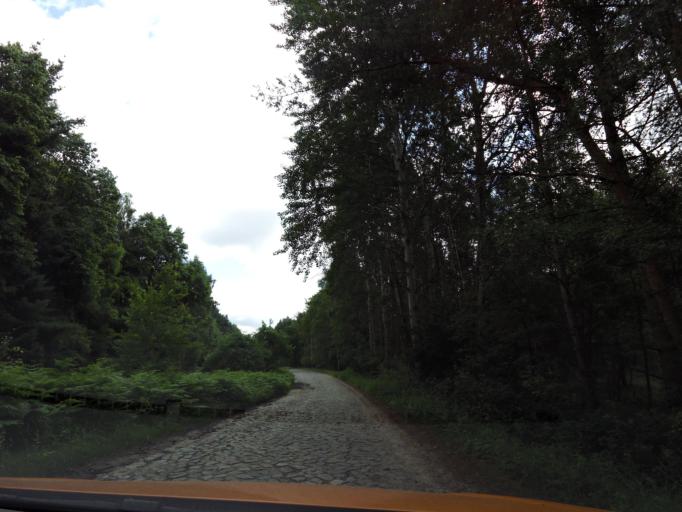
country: DE
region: Mecklenburg-Vorpommern
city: Krakow am See
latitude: 53.5907
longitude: 12.2651
